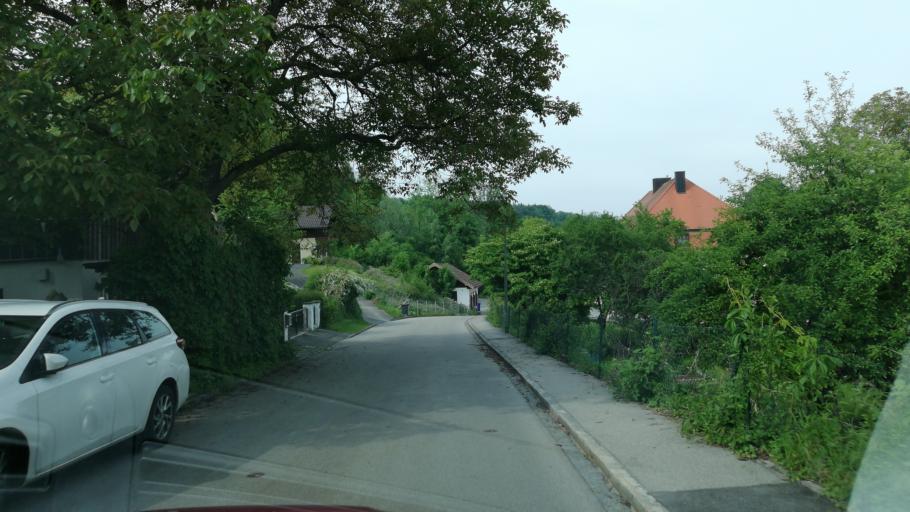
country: DE
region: Bavaria
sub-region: Upper Bavaria
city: Mehring
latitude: 48.1390
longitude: 12.7941
